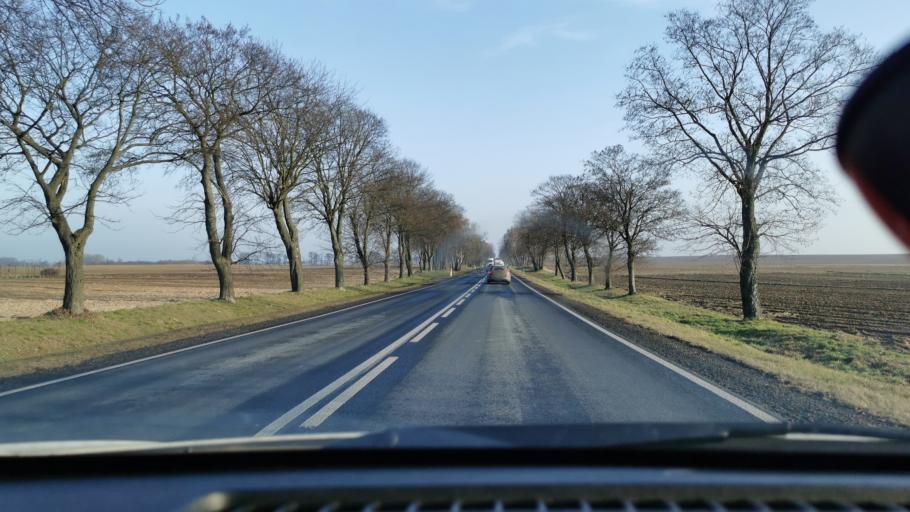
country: PL
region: Lodz Voivodeship
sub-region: Powiat sieradzki
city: Wroblew
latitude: 51.6233
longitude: 18.5756
